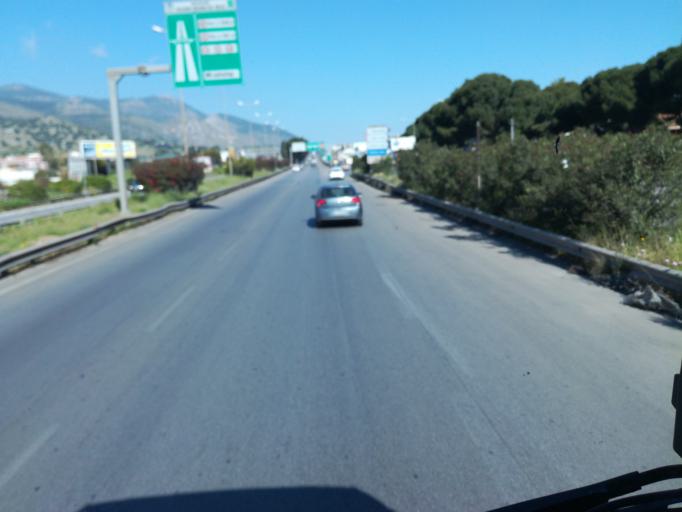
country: IT
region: Sicily
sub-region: Palermo
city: Palermo
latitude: 38.1511
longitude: 13.3235
